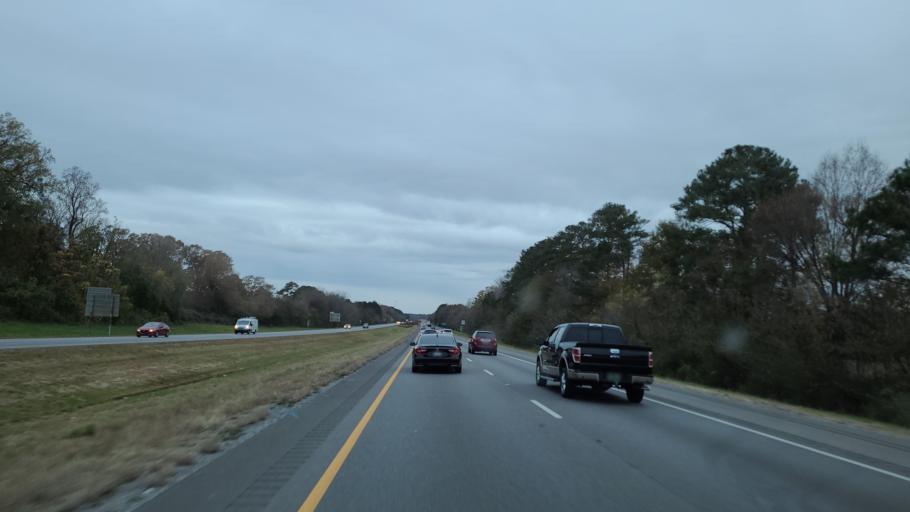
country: US
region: Alabama
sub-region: Jefferson County
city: Bessemer
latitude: 33.3370
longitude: -86.9312
